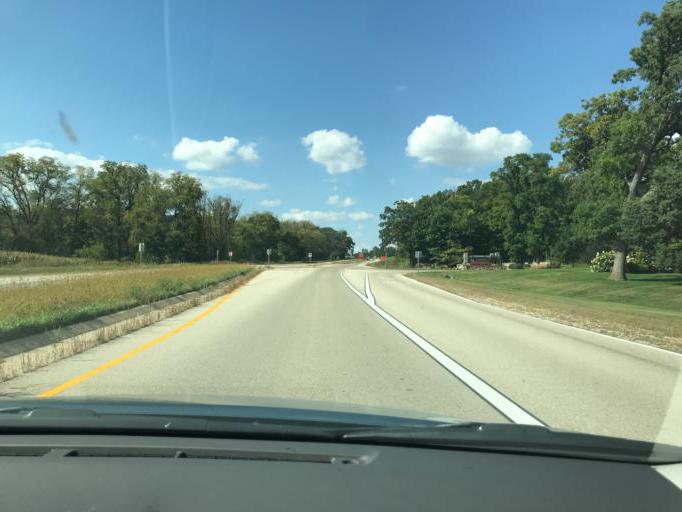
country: US
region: Wisconsin
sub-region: Walworth County
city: Williams Bay
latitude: 42.5931
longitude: -88.5347
